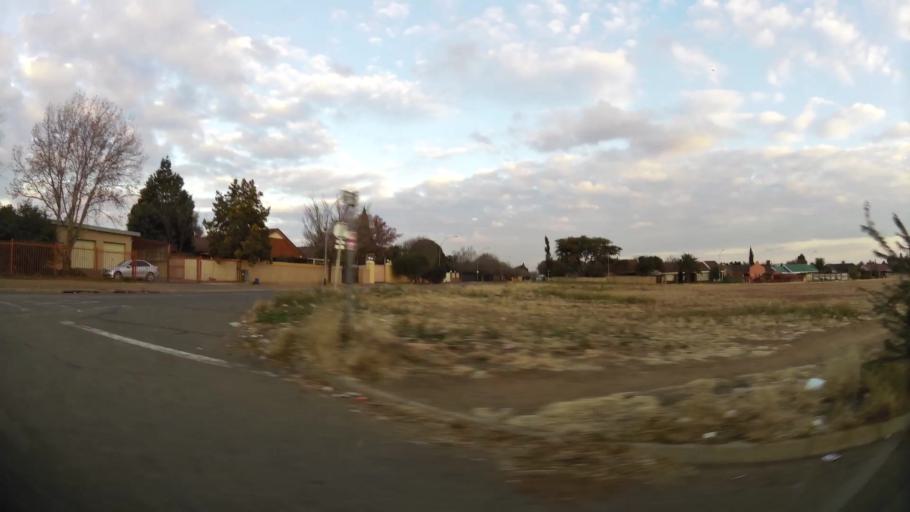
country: ZA
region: Orange Free State
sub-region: Mangaung Metropolitan Municipality
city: Bloemfontein
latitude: -29.1606
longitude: 26.1883
